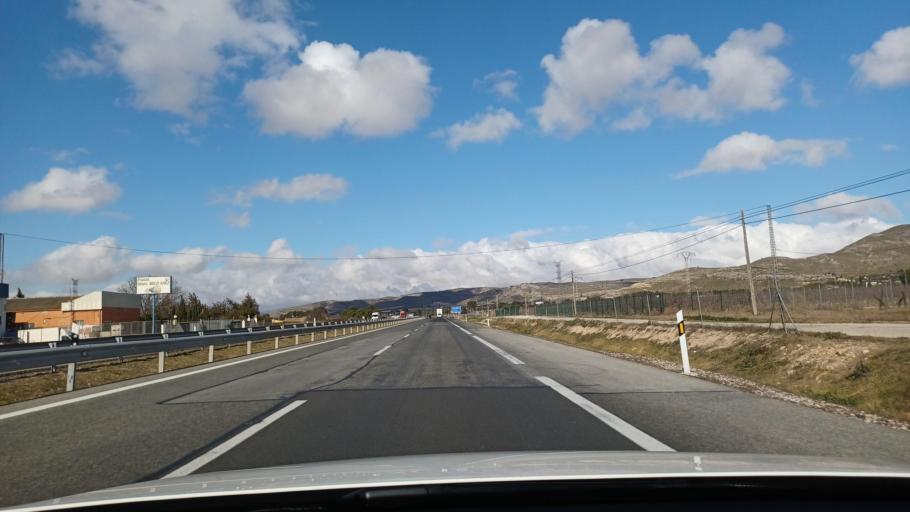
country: ES
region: Valencia
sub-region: Provincia de Alicante
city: Villena
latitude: 38.6592
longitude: -0.8777
